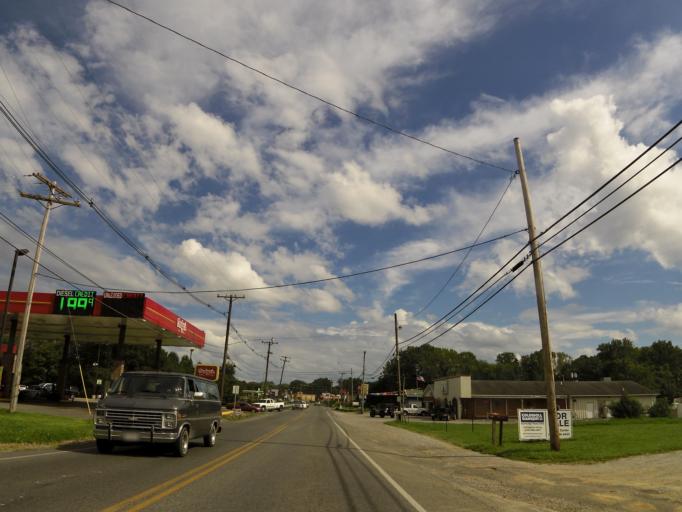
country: US
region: Kentucky
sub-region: Christian County
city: Hopkinsville
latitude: 36.8739
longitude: -87.5023
